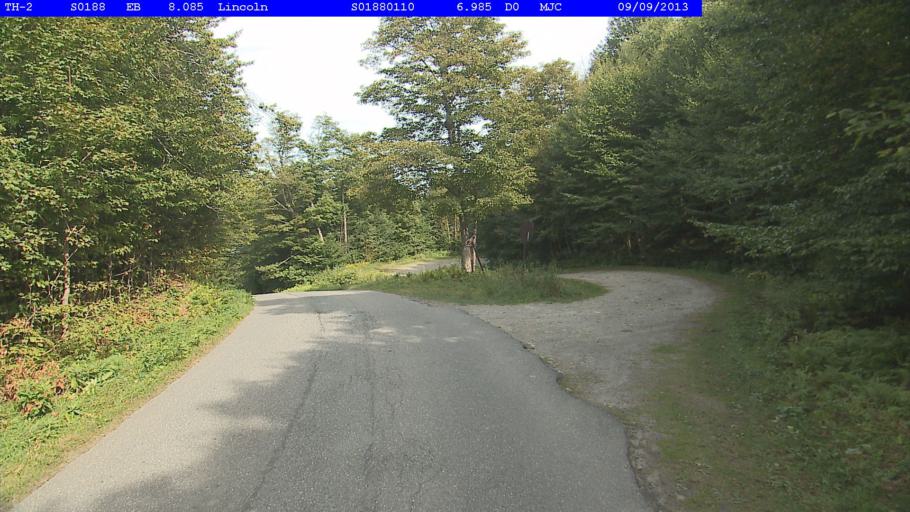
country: US
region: Vermont
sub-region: Addison County
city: Bristol
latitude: 44.0947
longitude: -72.9275
